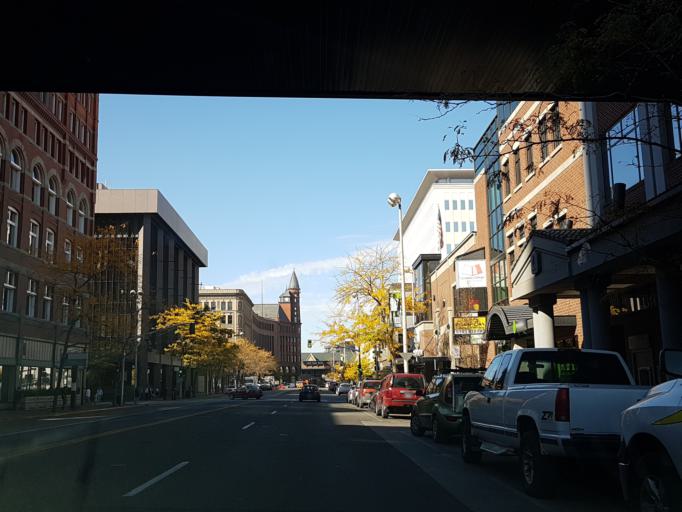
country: US
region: Washington
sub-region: Spokane County
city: Spokane
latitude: 47.6580
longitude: -117.4227
